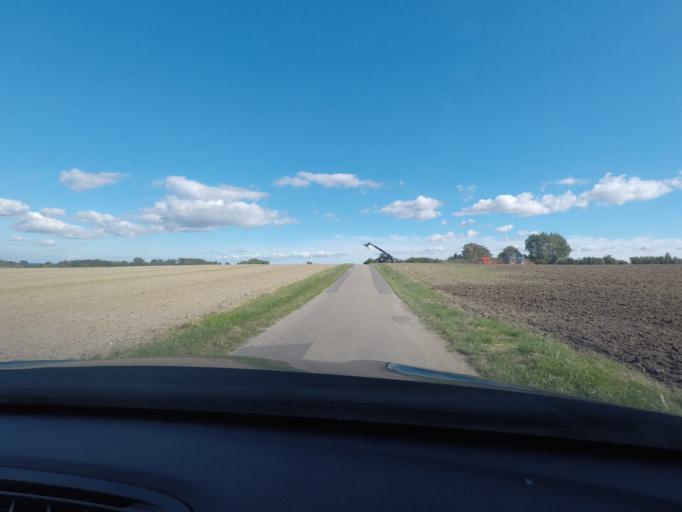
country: DK
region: Zealand
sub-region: Guldborgsund Kommune
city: Sakskobing
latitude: 54.9757
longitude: 11.5510
